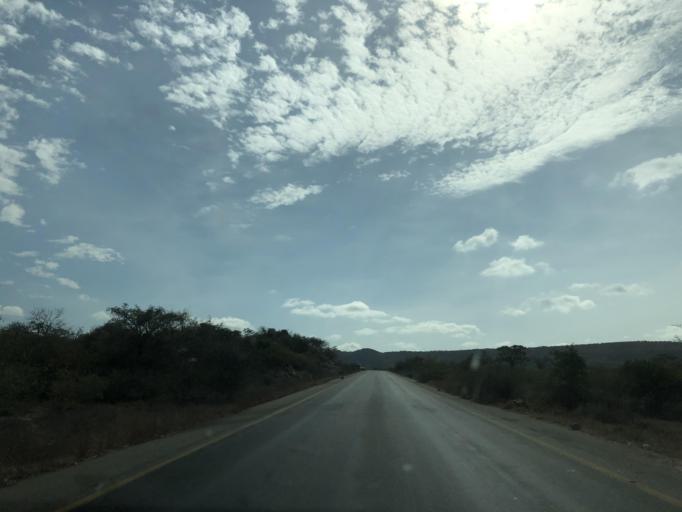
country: AO
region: Benguela
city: Benguela
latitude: -12.9802
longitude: 13.6208
